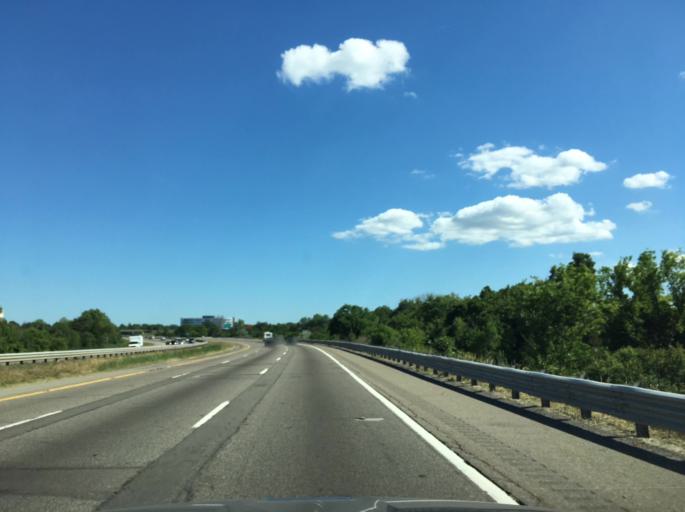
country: US
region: Michigan
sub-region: Oakland County
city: Troy
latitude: 42.5925
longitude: -83.1593
